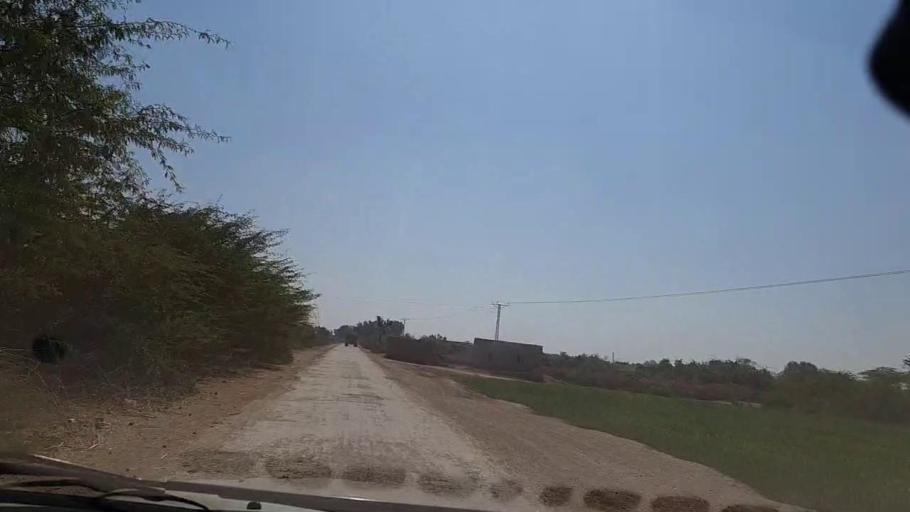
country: PK
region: Sindh
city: Mirpur Khas
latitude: 25.4781
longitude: 69.0479
